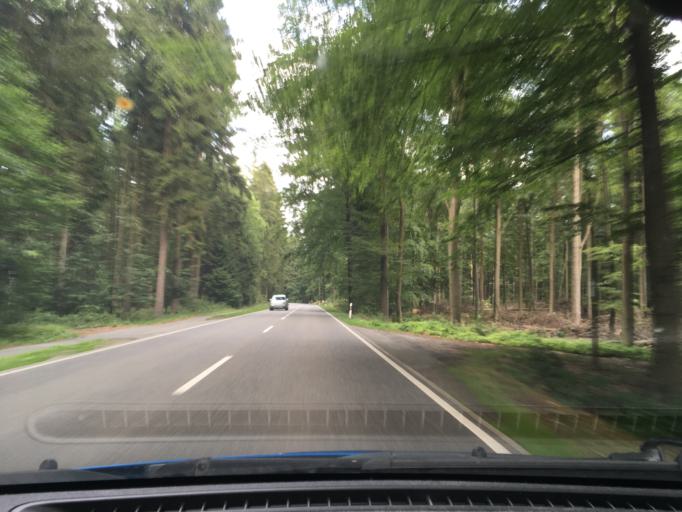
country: DE
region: Lower Saxony
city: Bendestorf
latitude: 53.3375
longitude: 9.9389
